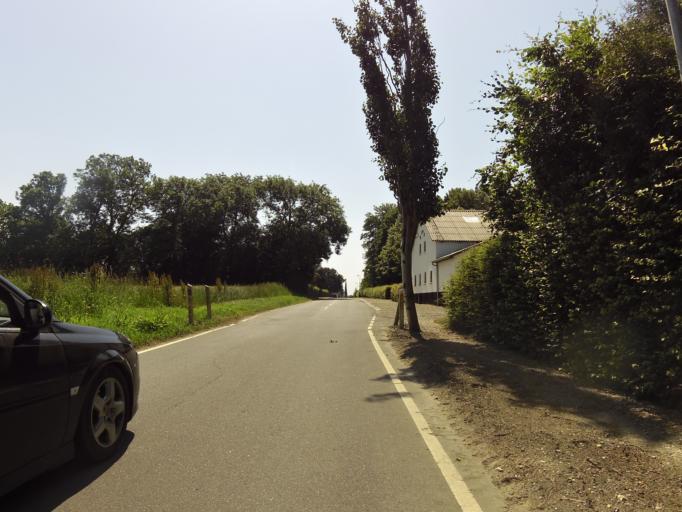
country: DK
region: South Denmark
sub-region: Haderslev Kommune
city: Vojens
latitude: 55.1608
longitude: 9.2155
